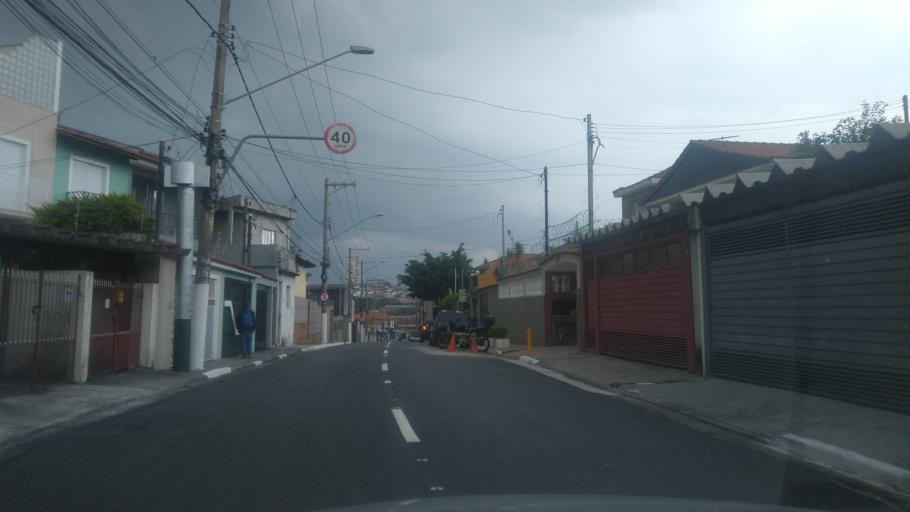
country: BR
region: Sao Paulo
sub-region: Sao Paulo
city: Sao Paulo
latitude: -23.4984
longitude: -46.6089
